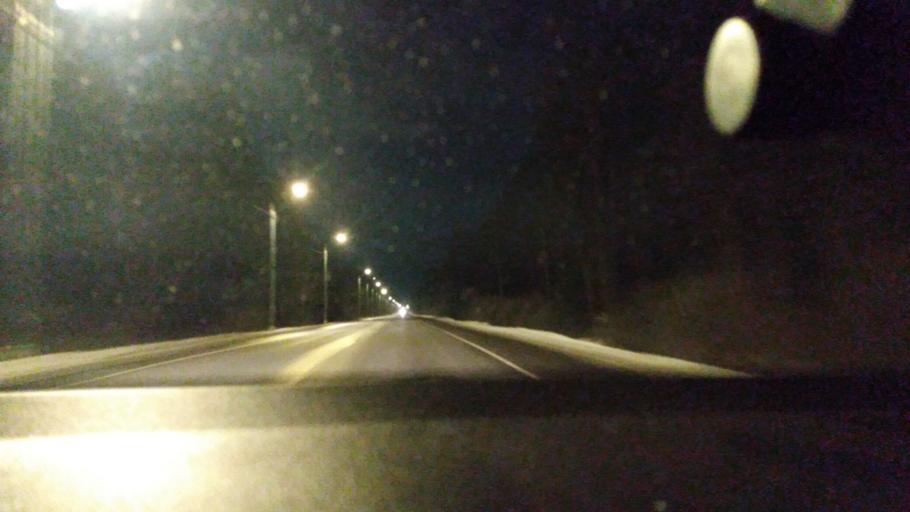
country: RU
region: Moskovskaya
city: Il'inskiy Pogost
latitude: 55.4570
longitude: 38.9907
